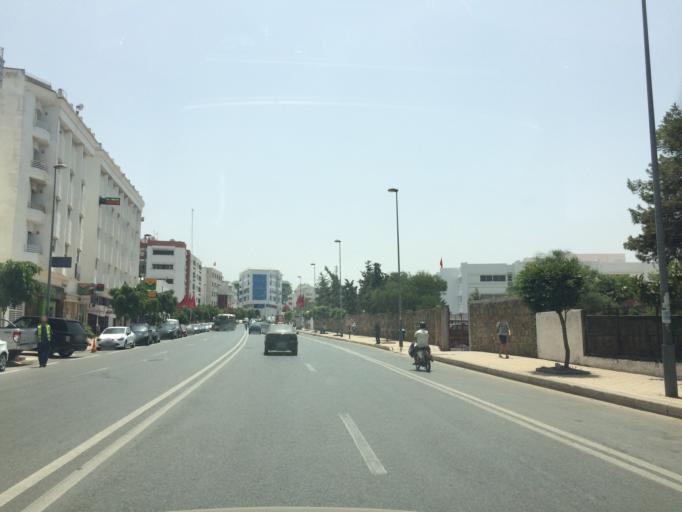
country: MA
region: Rabat-Sale-Zemmour-Zaer
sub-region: Rabat
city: Rabat
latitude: 34.0013
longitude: -6.8515
